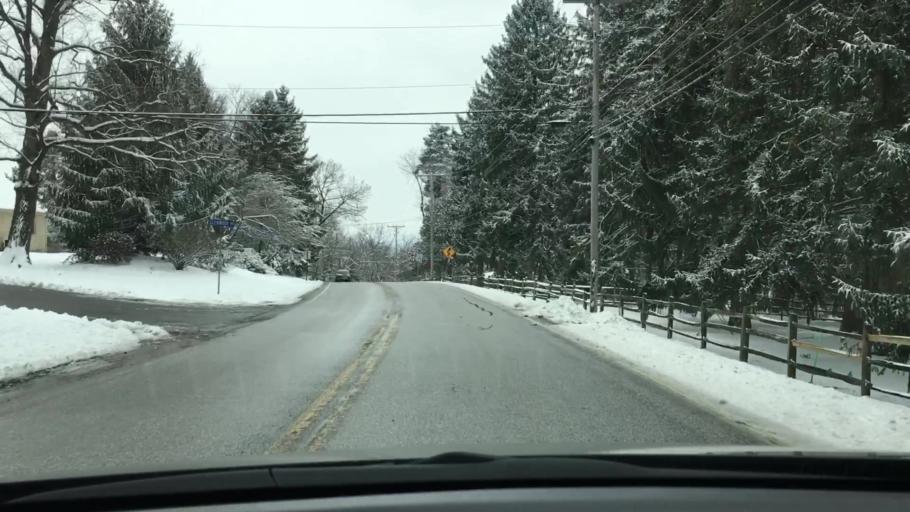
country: US
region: Pennsylvania
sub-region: York County
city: Grantley
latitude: 39.9376
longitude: -76.7271
